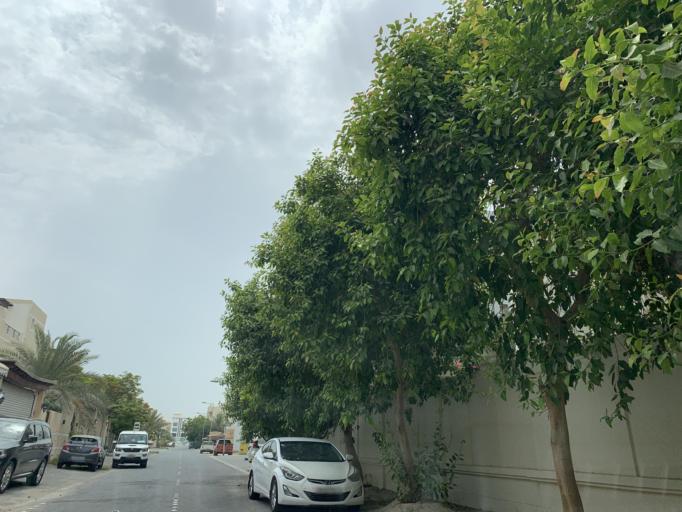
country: BH
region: Northern
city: Madinat `Isa
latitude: 26.1809
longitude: 50.4774
